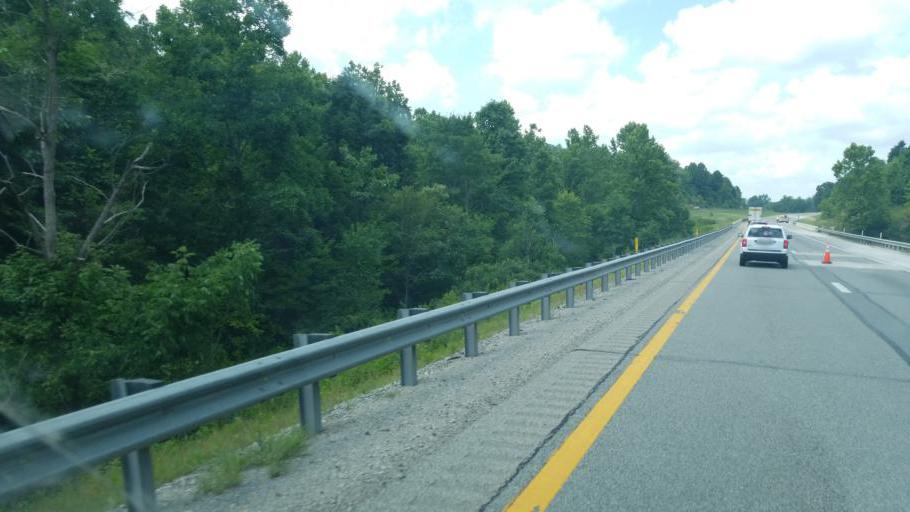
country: US
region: West Virginia
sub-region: Raleigh County
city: Prosperity
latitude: 37.8650
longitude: -81.2599
